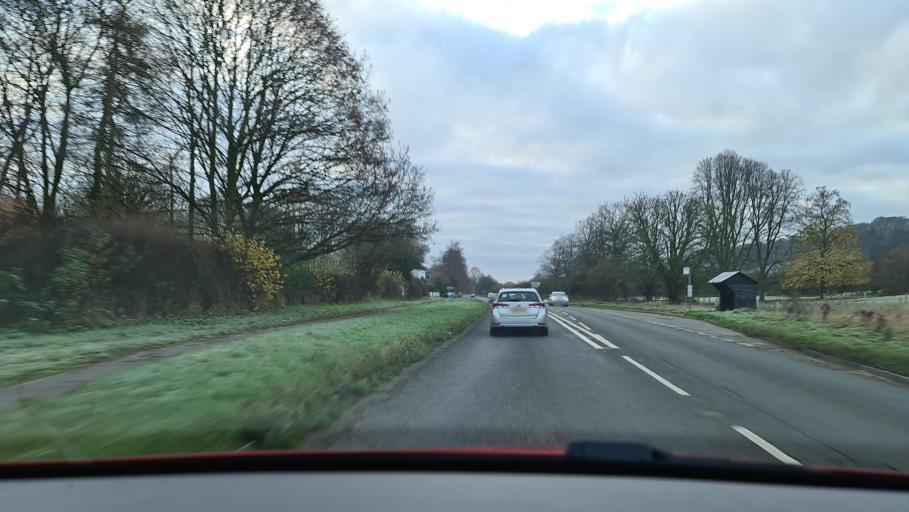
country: GB
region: England
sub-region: Buckinghamshire
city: Princes Risborough
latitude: 51.6668
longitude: -0.8115
